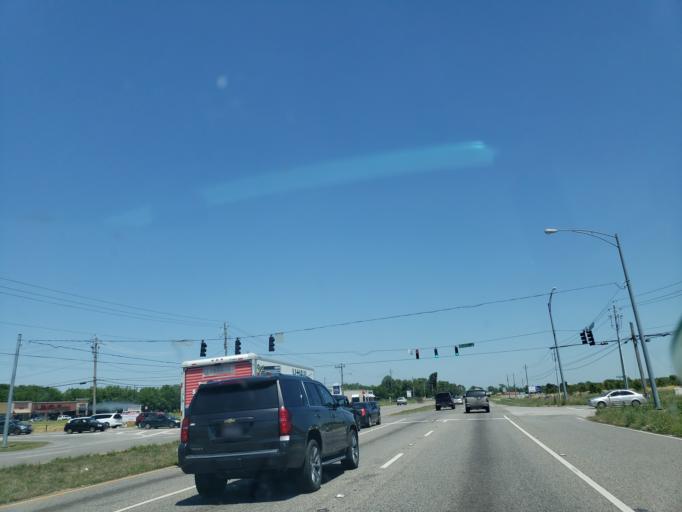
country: US
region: Alabama
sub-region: Madison County
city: Hazel Green
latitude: 34.9464
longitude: -86.5716
